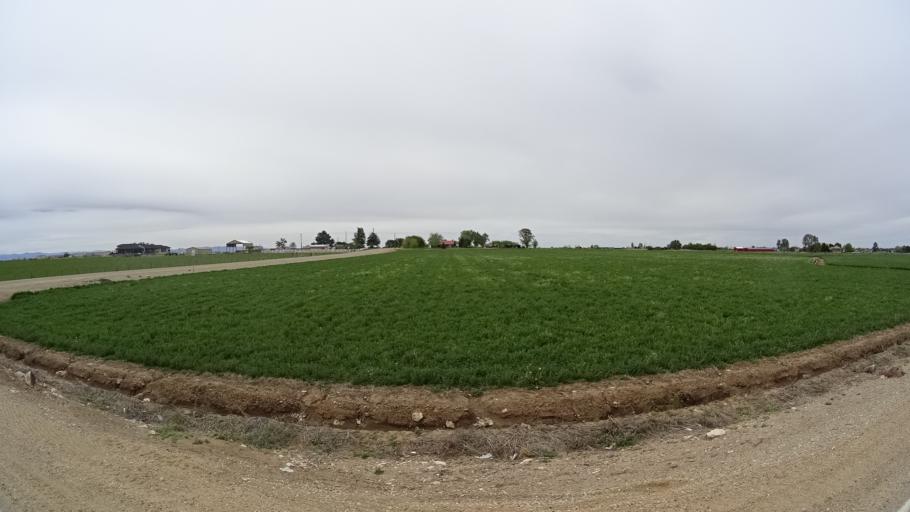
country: US
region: Idaho
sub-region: Ada County
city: Kuna
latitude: 43.4962
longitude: -116.3737
